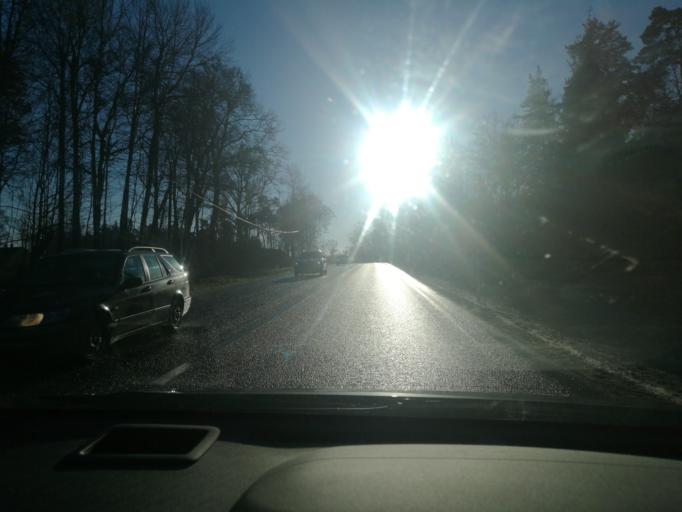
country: SE
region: Vaestmanland
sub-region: Kungsors Kommun
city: Kungsoer
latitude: 59.2722
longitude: 16.1182
